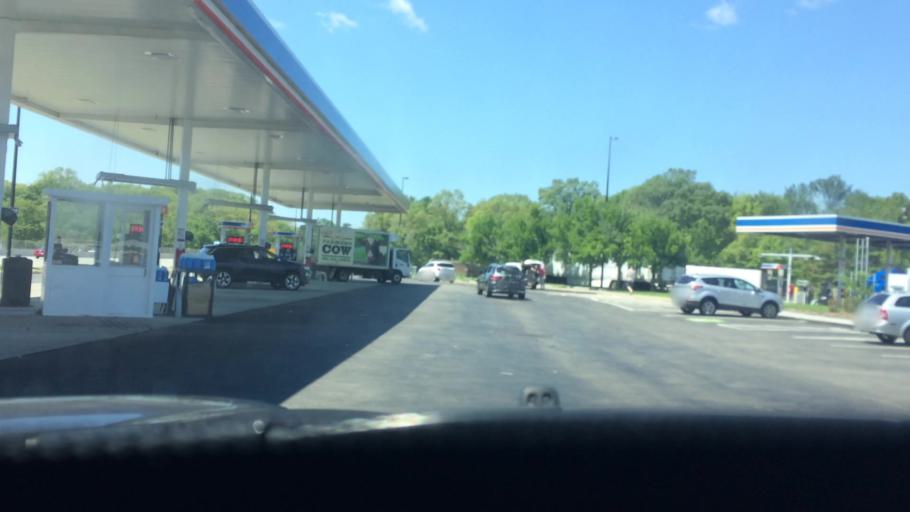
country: US
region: Massachusetts
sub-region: Middlesex County
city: Framingham Center
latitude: 42.3119
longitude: -71.4289
